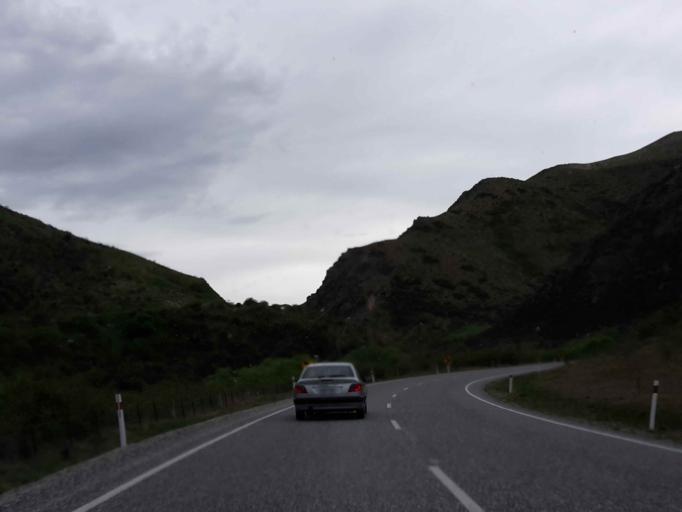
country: NZ
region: Otago
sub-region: Queenstown-Lakes District
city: Wanaka
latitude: -44.7358
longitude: 169.5068
